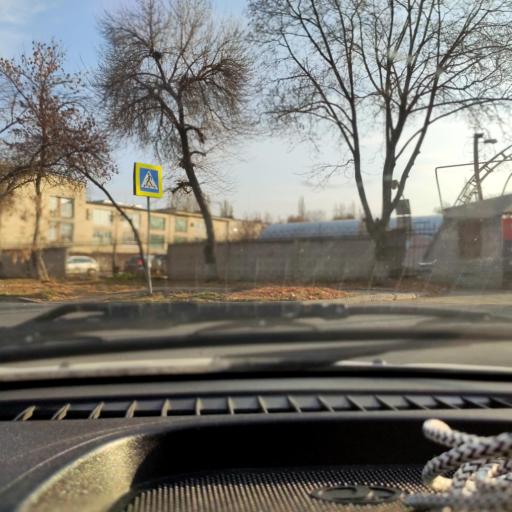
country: RU
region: Samara
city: Tol'yatti
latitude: 53.5011
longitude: 49.3934
